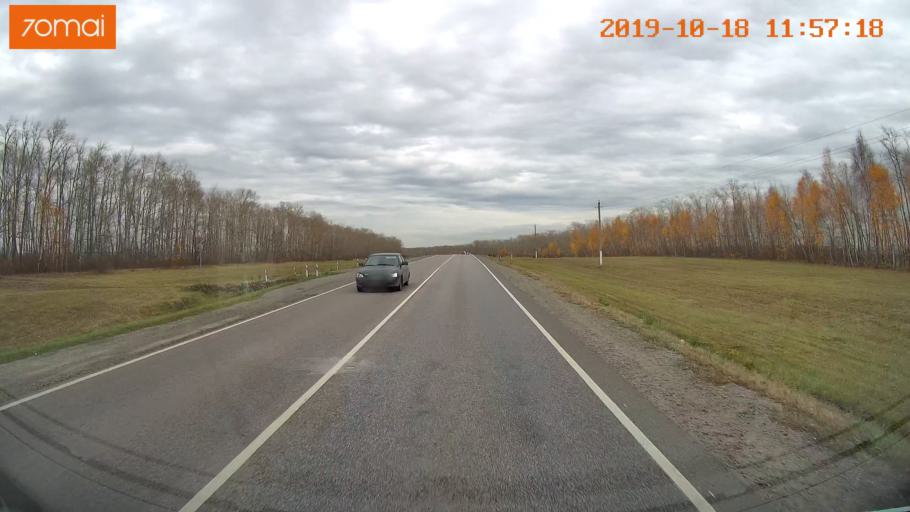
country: RU
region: Rjazan
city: Mikhaylov
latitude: 54.2663
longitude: 39.1401
